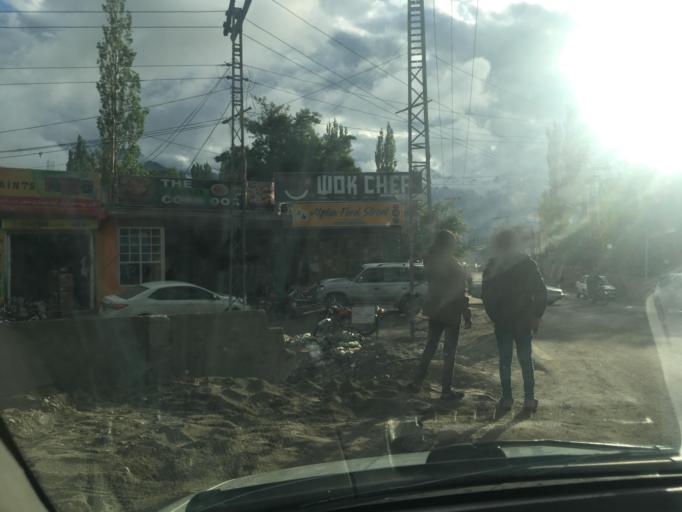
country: PK
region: Gilgit-Baltistan
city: Skardu
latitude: 35.2899
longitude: 75.6409
